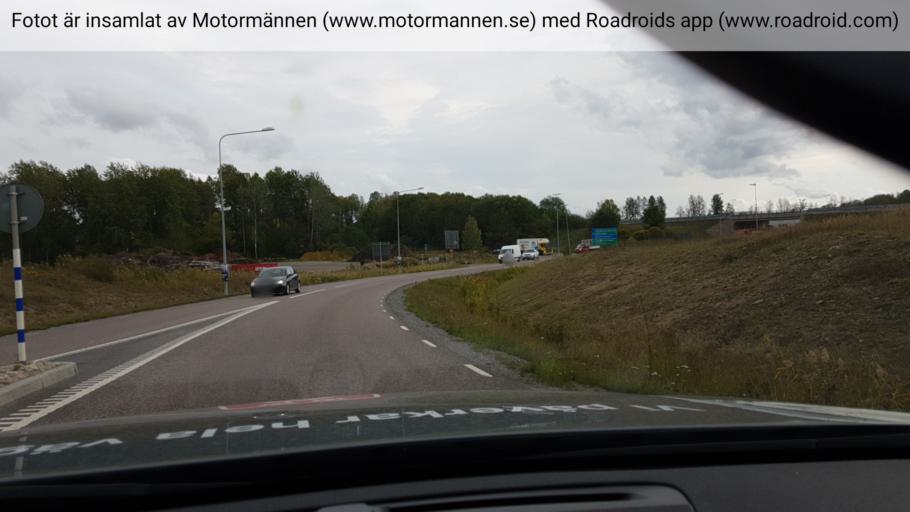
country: SE
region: Stockholm
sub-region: Norrtalje Kommun
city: Norrtalje
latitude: 59.7435
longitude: 18.6887
